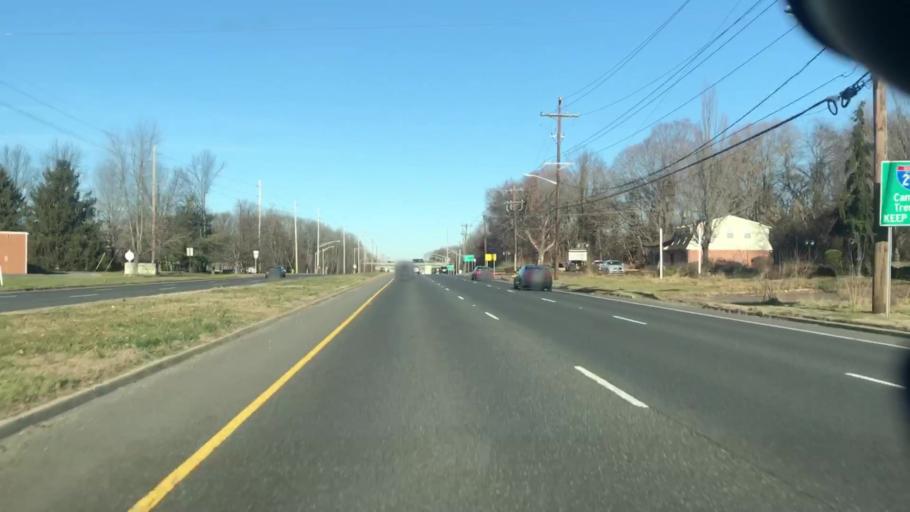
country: US
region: New Jersey
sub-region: Burlington County
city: Willingboro
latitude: 40.0410
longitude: -74.8308
